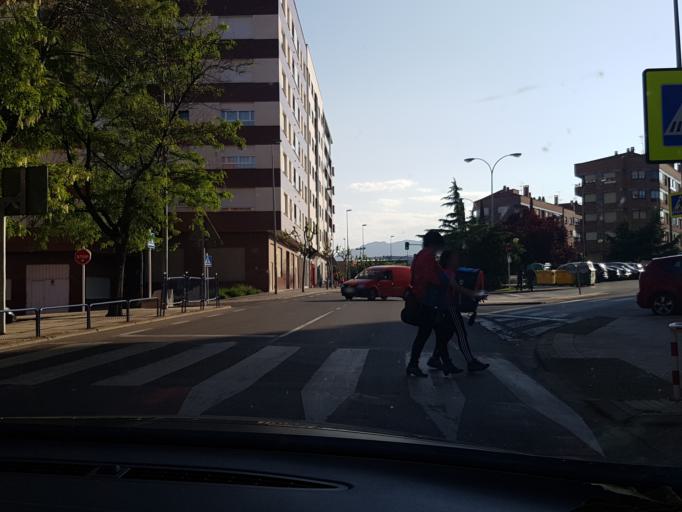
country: ES
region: La Rioja
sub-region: Provincia de La Rioja
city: Arnedo
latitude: 42.2235
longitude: -2.1033
